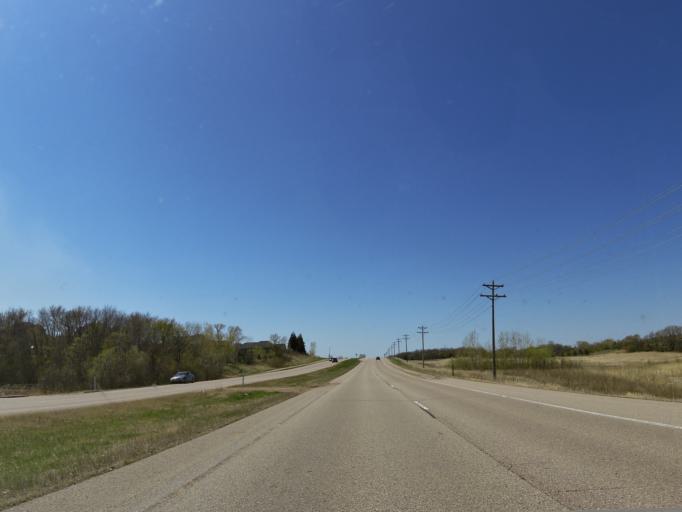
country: US
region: Minnesota
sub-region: Scott County
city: Prior Lake
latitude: 44.7468
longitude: -93.4584
